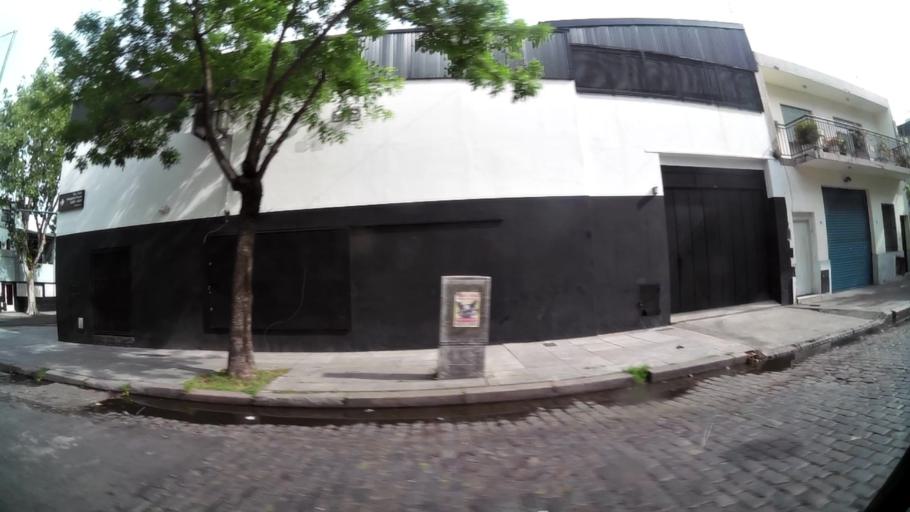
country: AR
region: Buenos Aires F.D.
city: Buenos Aires
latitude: -34.6406
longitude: -58.4171
